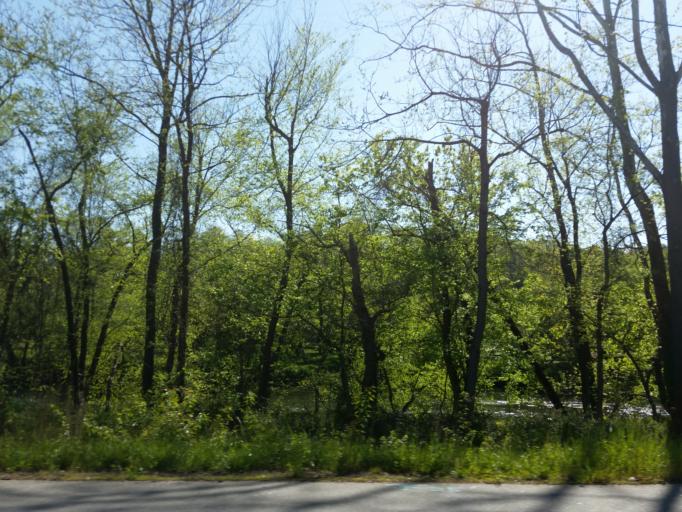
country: US
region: North Carolina
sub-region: Buncombe County
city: Asheville
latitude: 35.5725
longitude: -82.5640
